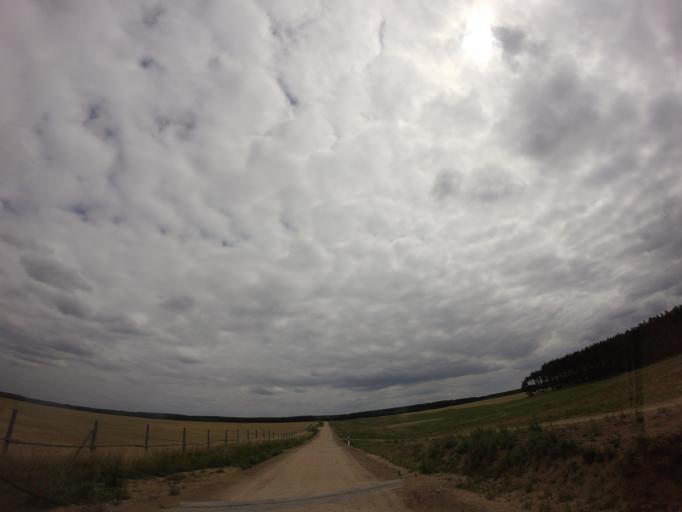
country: PL
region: Lubusz
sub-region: Powiat strzelecko-drezdenecki
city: Zwierzyn
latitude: 52.8818
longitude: 15.6029
